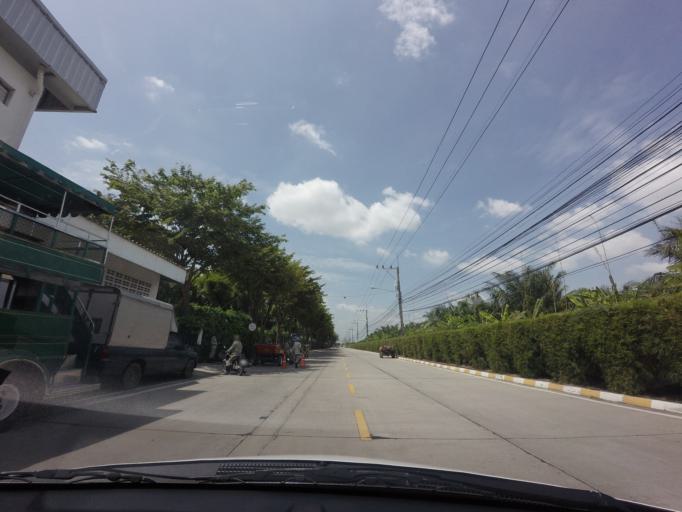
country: TH
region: Pathum Thani
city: Thanyaburi
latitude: 13.9905
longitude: 100.6745
